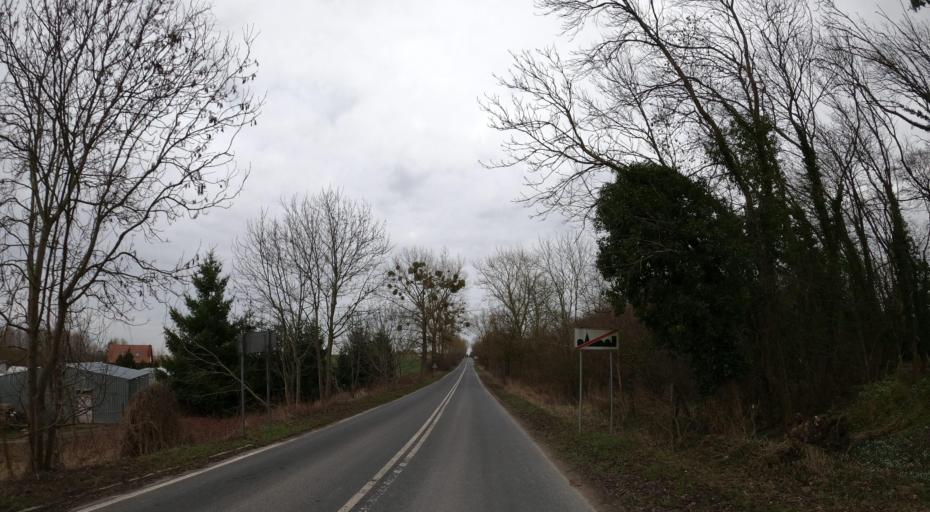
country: PL
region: West Pomeranian Voivodeship
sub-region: Powiat policki
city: Przeclaw
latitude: 53.3484
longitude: 14.4788
